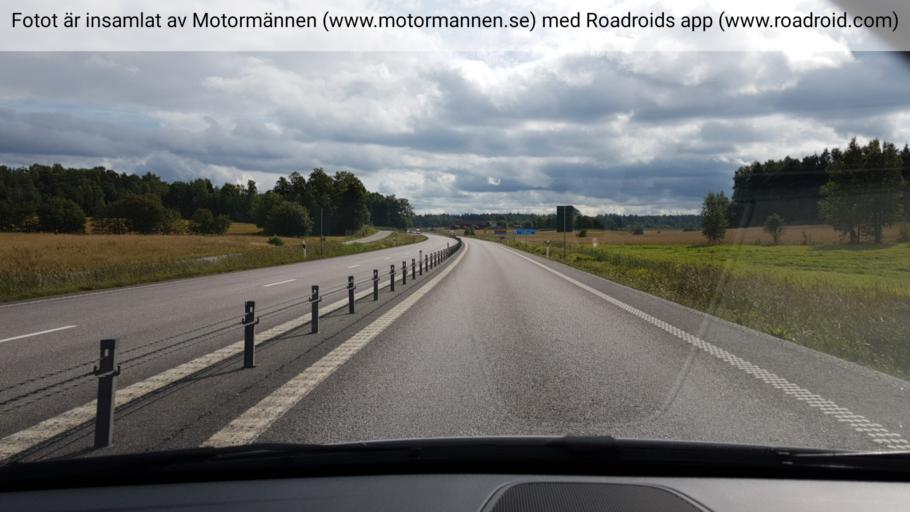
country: SE
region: Vaestra Goetaland
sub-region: Vanersborgs Kommun
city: Vargon
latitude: 58.2827
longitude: 12.4353
